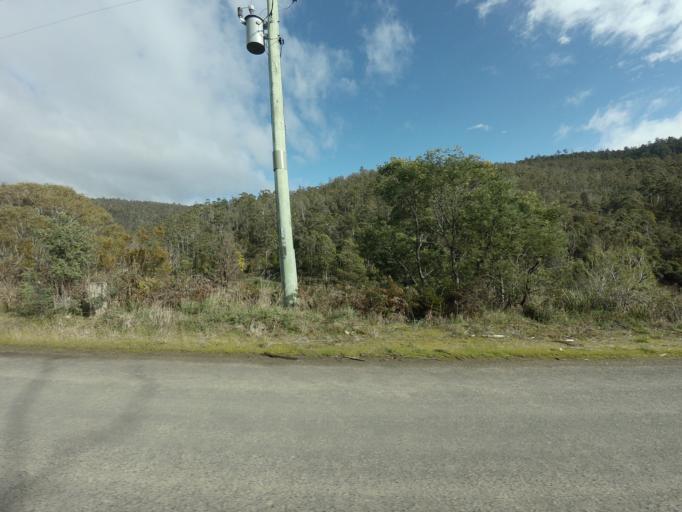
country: AU
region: Tasmania
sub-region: Derwent Valley
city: New Norfolk
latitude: -42.7872
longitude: 146.9468
